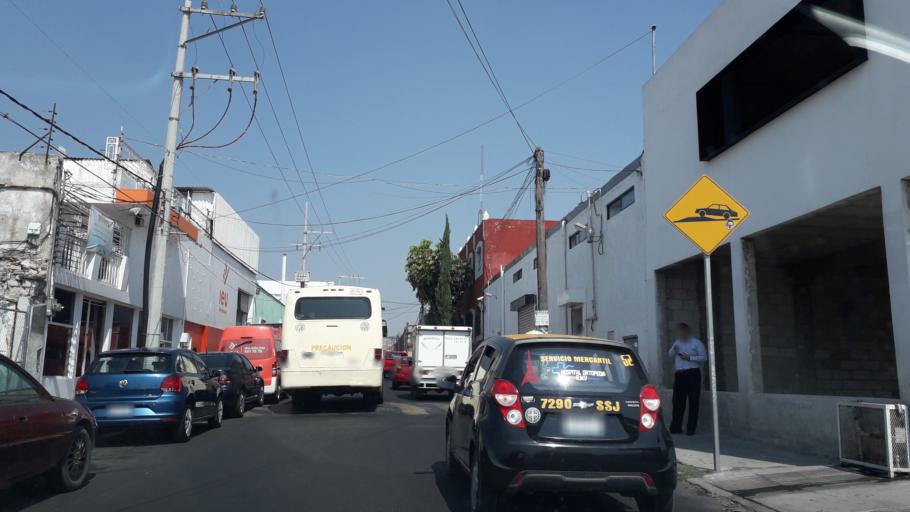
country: MX
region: Puebla
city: Puebla
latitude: 19.0523
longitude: -98.2118
